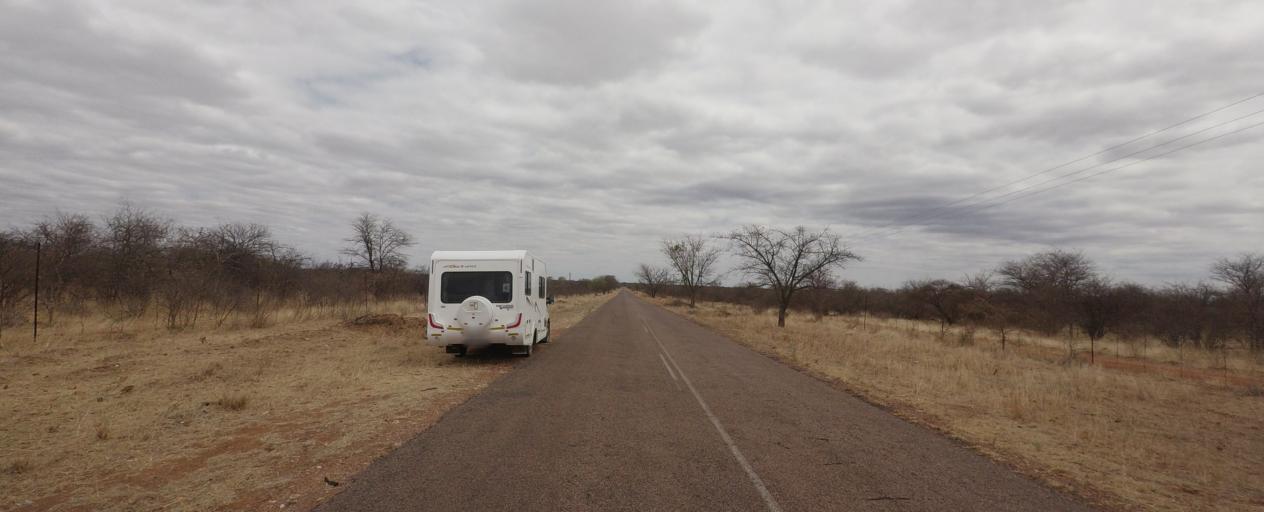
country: BW
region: Central
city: Makobeng
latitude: -22.9232
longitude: 28.1706
